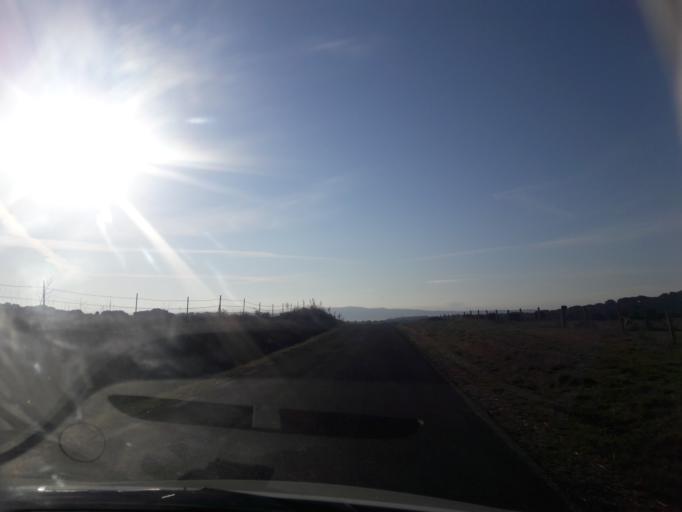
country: ES
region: Castille and Leon
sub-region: Provincia de Salamanca
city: Montejo
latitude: 40.6261
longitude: -5.6147
